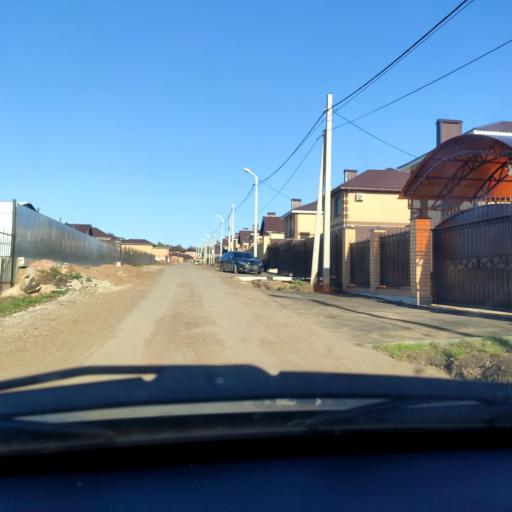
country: RU
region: Bashkortostan
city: Mikhaylovka
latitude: 54.8325
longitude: 55.8718
